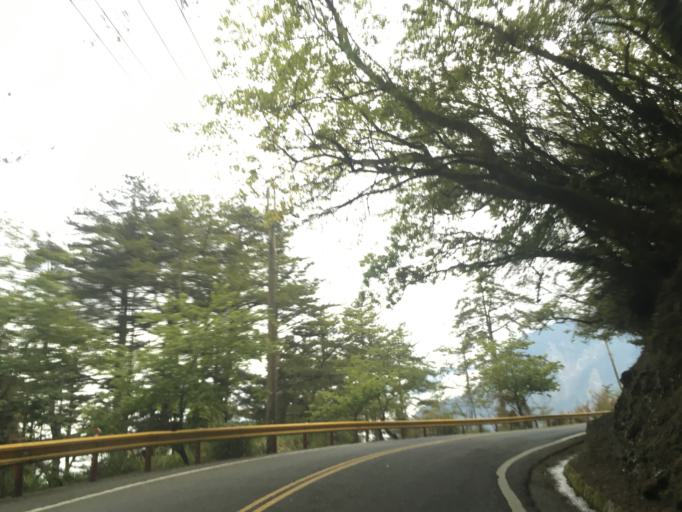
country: TW
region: Taiwan
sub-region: Hualien
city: Hualian
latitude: 24.1849
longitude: 121.3263
